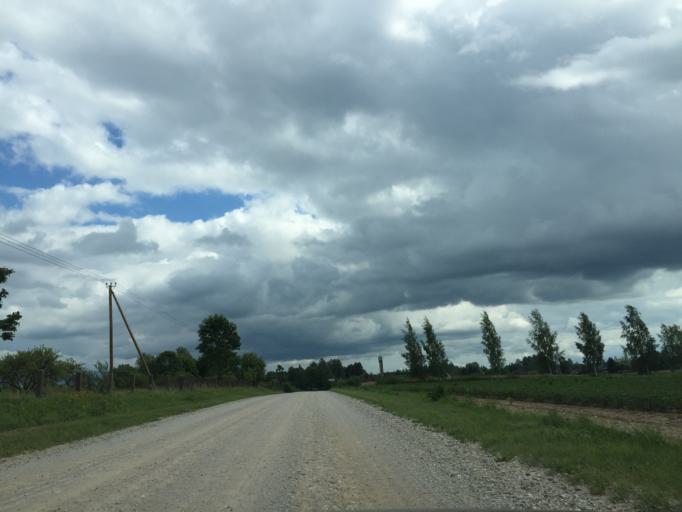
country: LV
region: Malpils
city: Malpils
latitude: 56.8646
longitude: 25.0137
